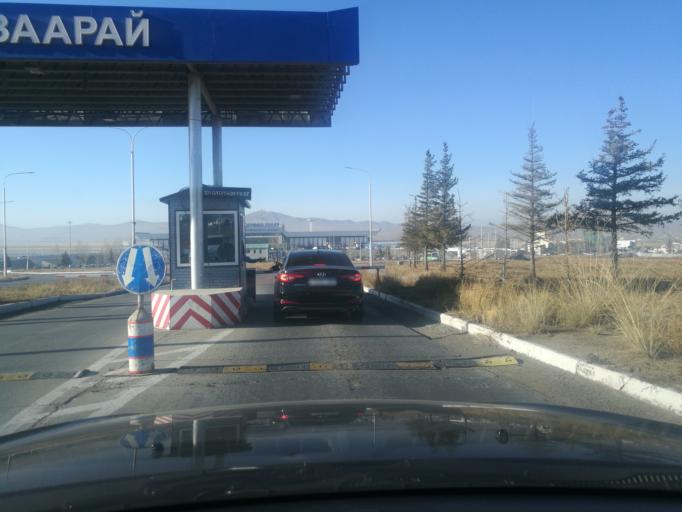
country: MN
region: Ulaanbaatar
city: Ulaanbaatar
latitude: 47.8549
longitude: 106.7663
